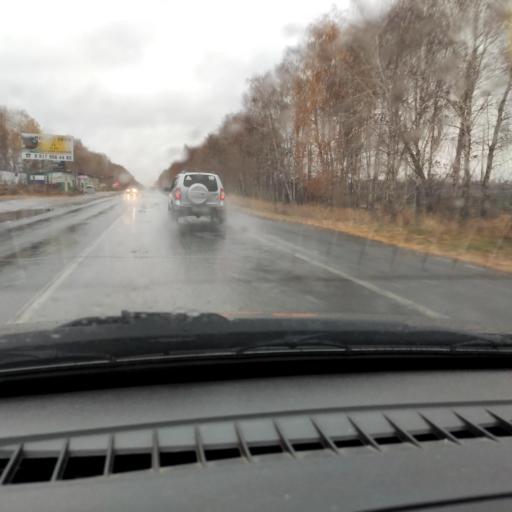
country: RU
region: Samara
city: Tol'yatti
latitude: 53.5898
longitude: 49.3298
